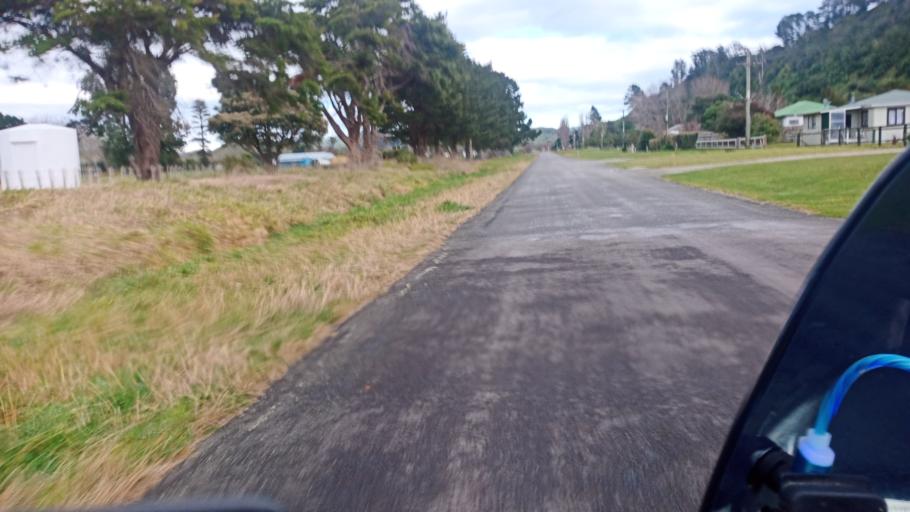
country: NZ
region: Gisborne
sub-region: Gisborne District
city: Gisborne
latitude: -38.3668
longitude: 178.3002
